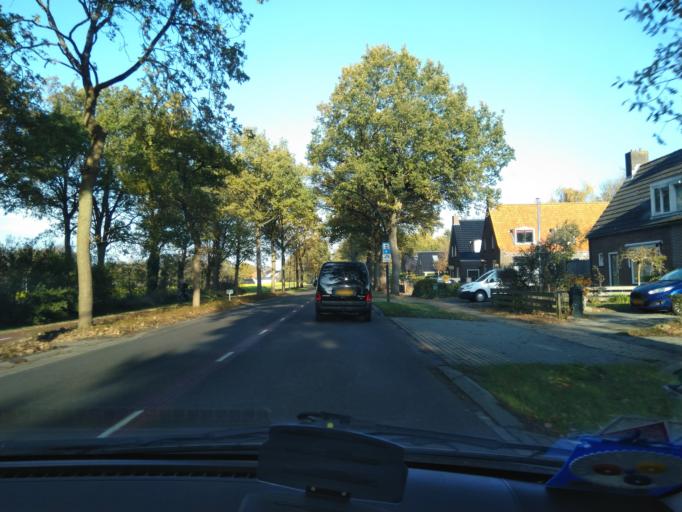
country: NL
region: Drenthe
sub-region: Gemeente Tynaarlo
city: Zuidlaren
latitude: 53.1164
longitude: 6.7187
